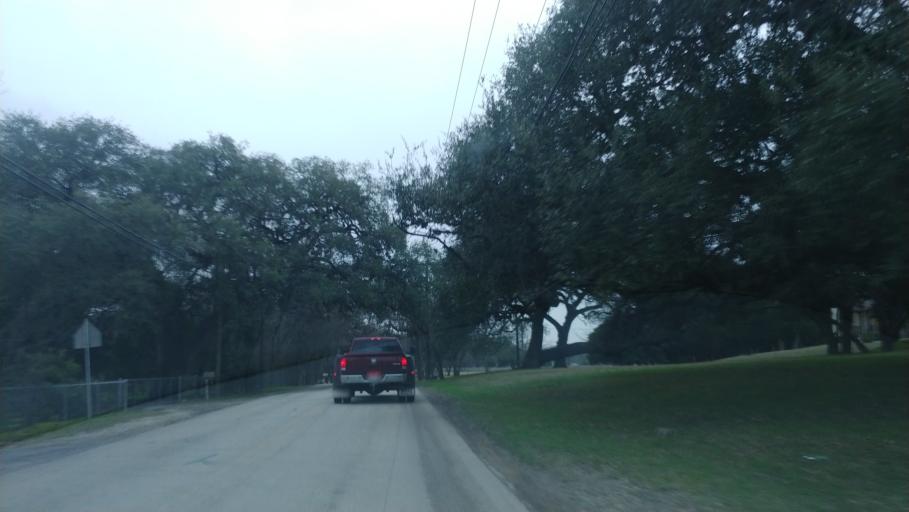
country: US
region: Texas
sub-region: Bexar County
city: Helotes
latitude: 29.6141
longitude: -98.6848
